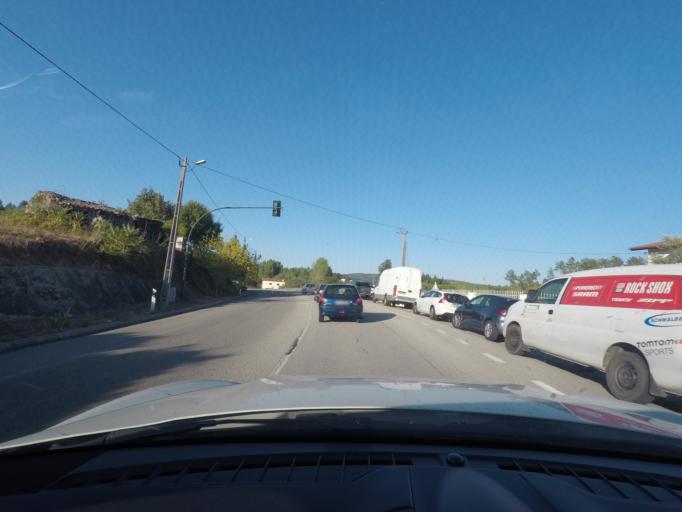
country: PT
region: Coimbra
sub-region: Vila Nova de Poiares
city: Poiares
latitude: 40.1815
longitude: -8.2620
